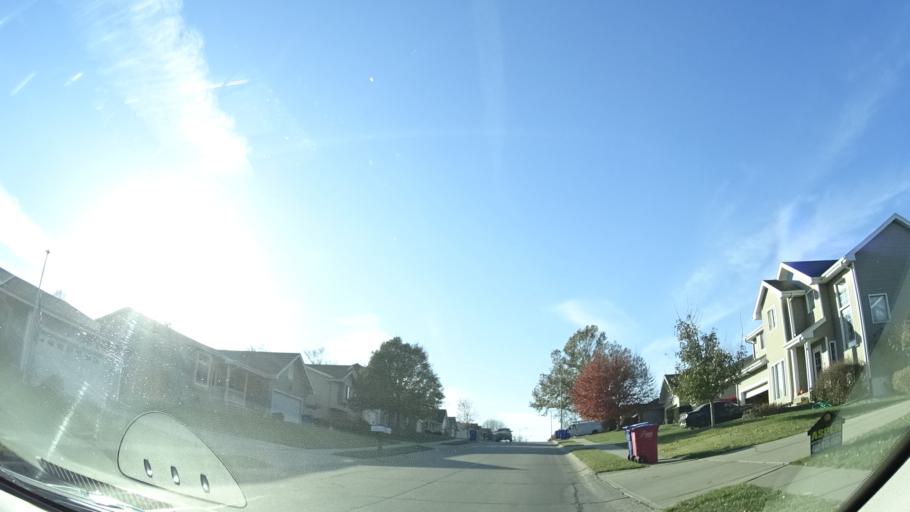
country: US
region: Nebraska
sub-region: Sarpy County
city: Offutt Air Force Base
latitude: 41.1333
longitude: -95.9481
